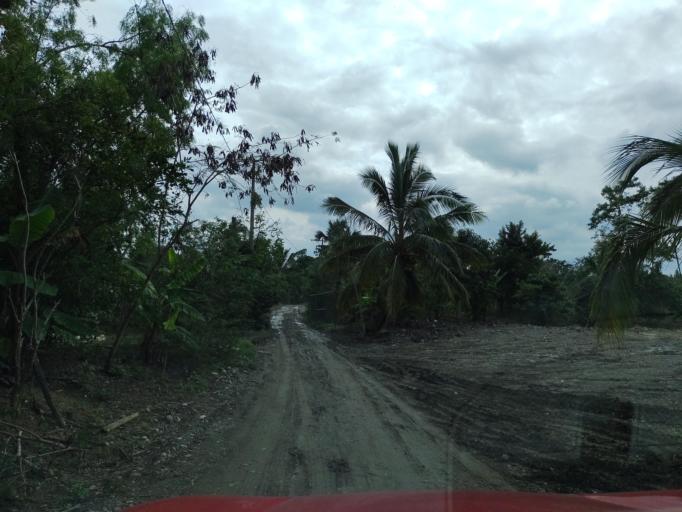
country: MX
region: Veracruz
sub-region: Papantla
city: El Chote
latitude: 20.4374
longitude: -97.3766
